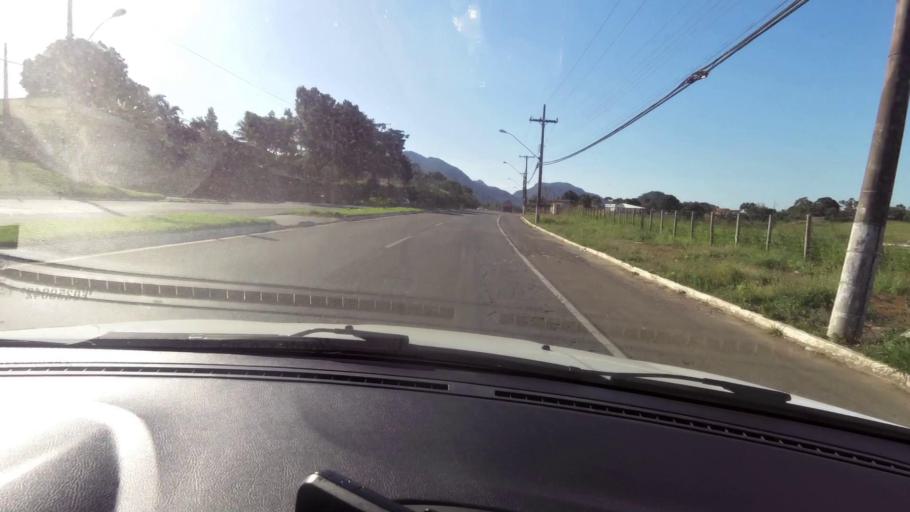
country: BR
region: Espirito Santo
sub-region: Guarapari
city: Guarapari
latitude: -20.6416
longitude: -40.5177
